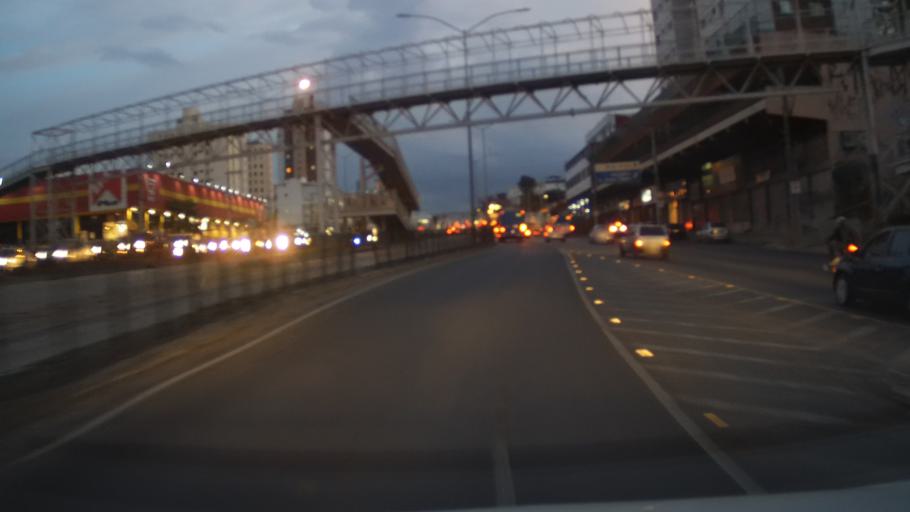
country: BR
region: Minas Gerais
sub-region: Belo Horizonte
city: Belo Horizonte
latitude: -19.8958
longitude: -43.9269
